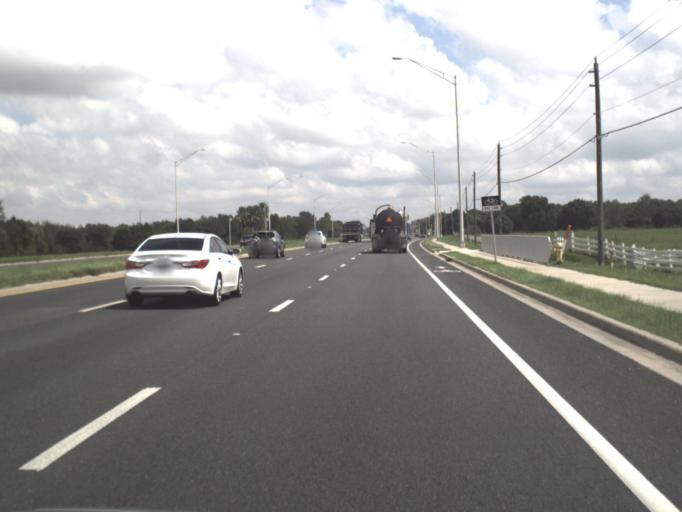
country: US
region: Florida
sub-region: Manatee County
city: Ellenton
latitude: 27.4858
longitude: -82.4523
